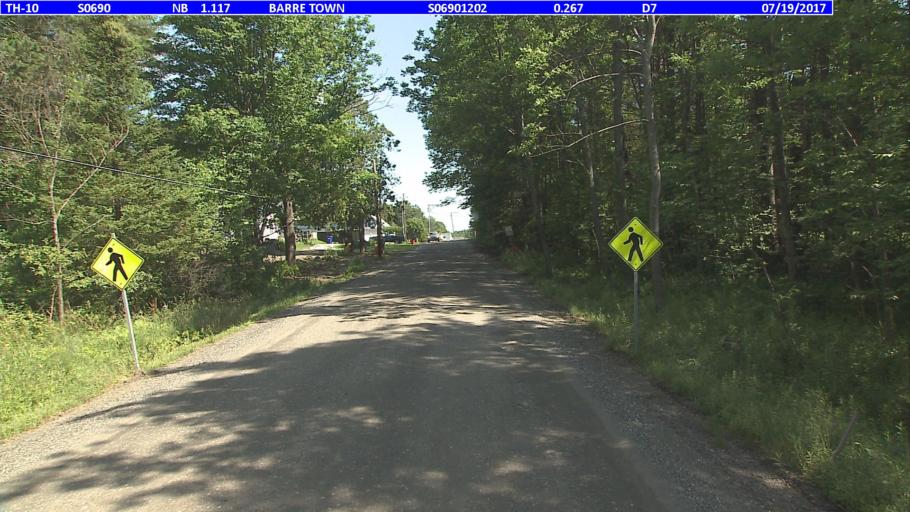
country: US
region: Vermont
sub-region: Washington County
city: South Barre
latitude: 44.1476
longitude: -72.4932
